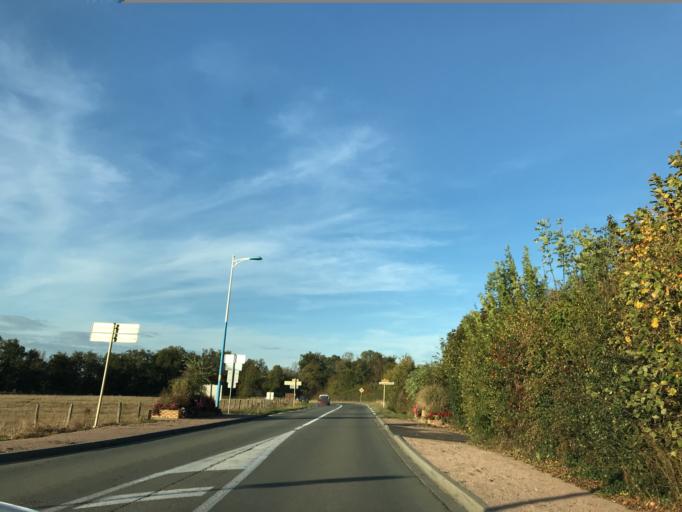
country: FR
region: Auvergne
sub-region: Departement du Puy-de-Dome
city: Puy-Guillaume
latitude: 45.9686
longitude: 3.4789
